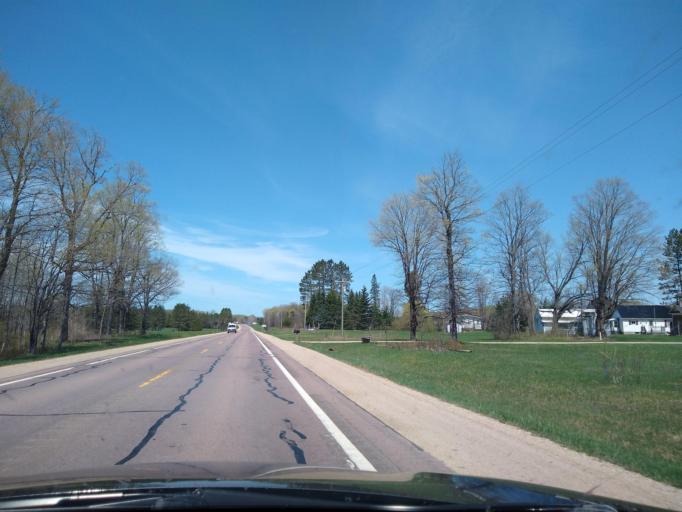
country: US
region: Michigan
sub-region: Marquette County
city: K. I. Sawyer Air Force Base
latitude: 46.2453
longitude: -87.0794
